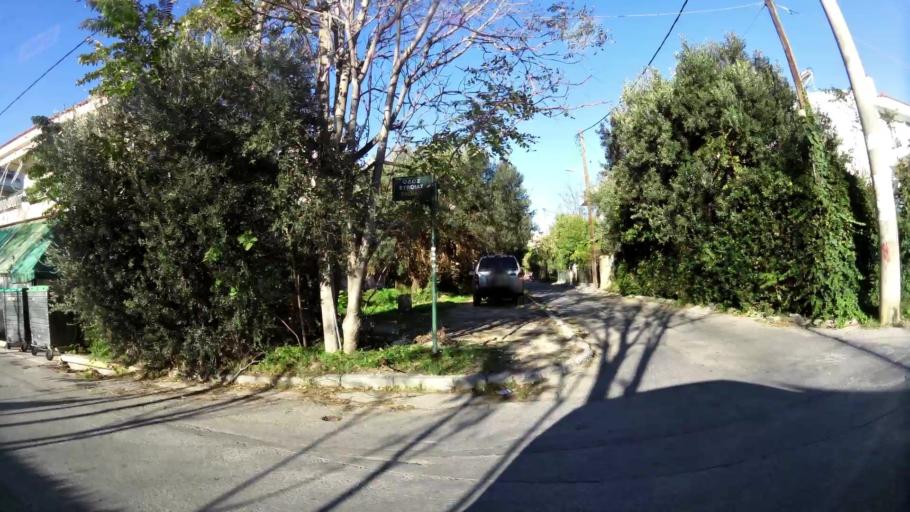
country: GR
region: Attica
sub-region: Nomarchia Anatolikis Attikis
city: Gerakas
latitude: 38.0085
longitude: 23.8631
